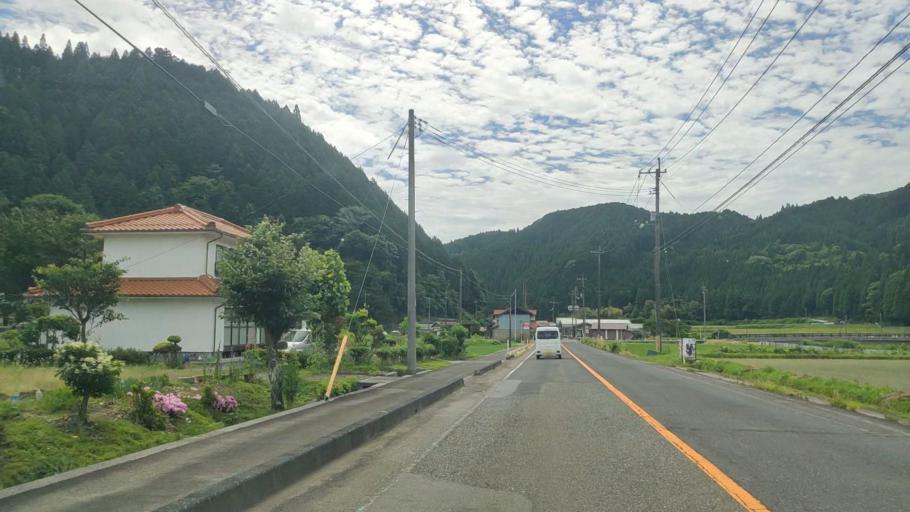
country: JP
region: Okayama
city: Niimi
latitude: 35.1581
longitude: 133.6132
